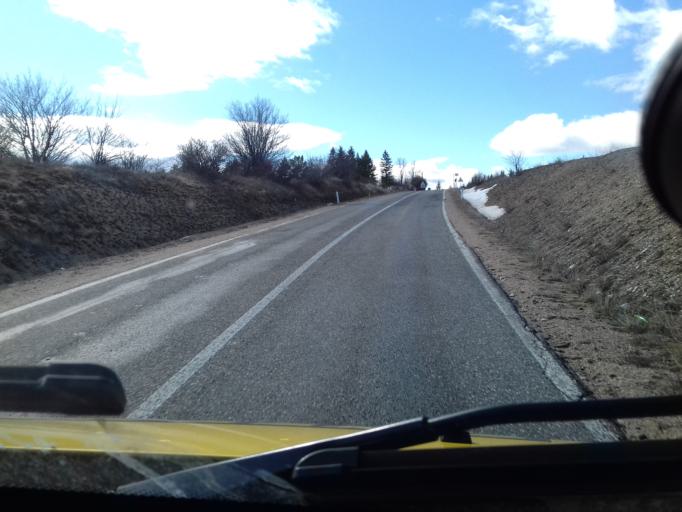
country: BA
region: Federation of Bosnia and Herzegovina
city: Tomislavgrad
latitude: 43.7349
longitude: 17.2229
